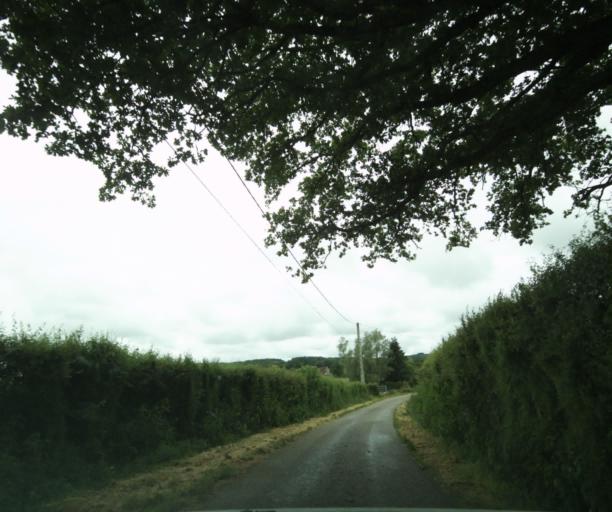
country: FR
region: Bourgogne
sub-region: Departement de Saone-et-Loire
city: Charolles
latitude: 46.4818
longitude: 4.3236
